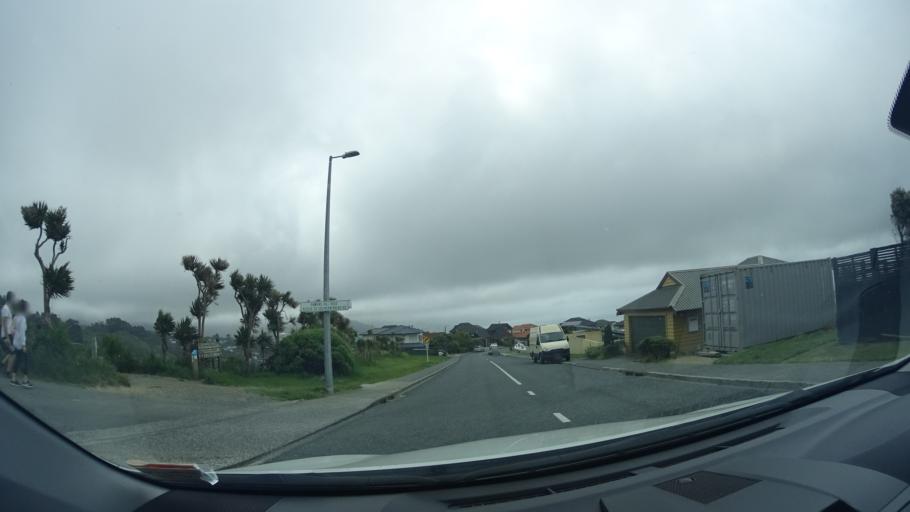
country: NZ
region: Wellington
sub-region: Wellington City
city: Brooklyn
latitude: -41.3045
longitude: 174.7539
